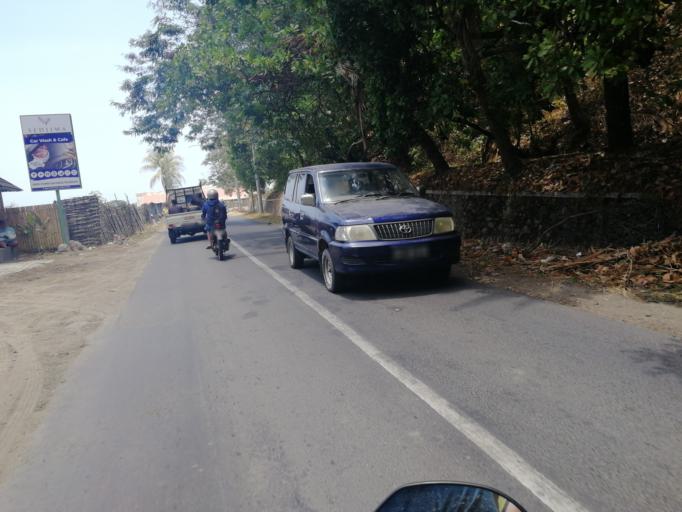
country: ID
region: West Nusa Tenggara
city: Karangsubagan
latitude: -8.4107
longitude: 116.0997
